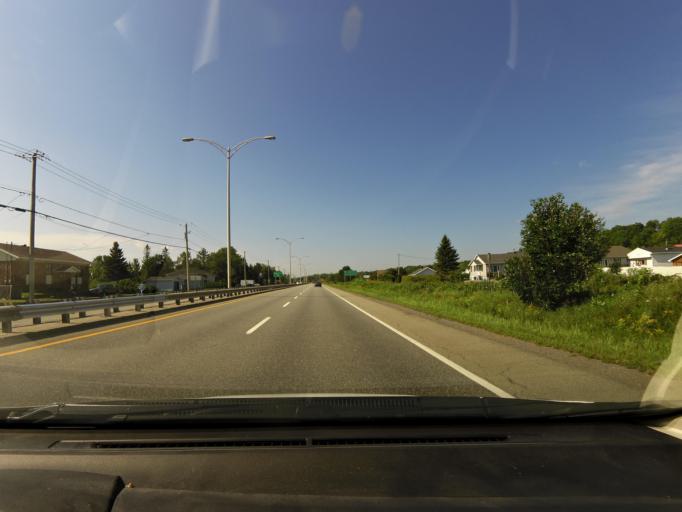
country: CA
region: Quebec
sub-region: Capitale-Nationale
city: Chateau-Richer
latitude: 46.9580
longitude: -71.0359
